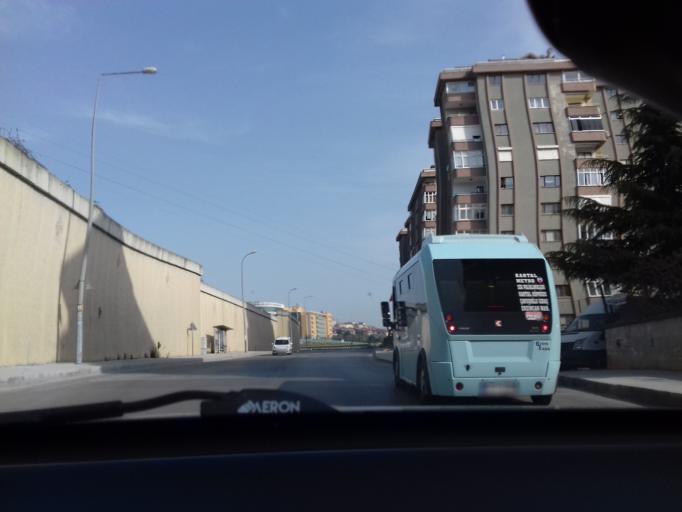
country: TR
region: Istanbul
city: Pendik
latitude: 40.9091
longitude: 29.2363
